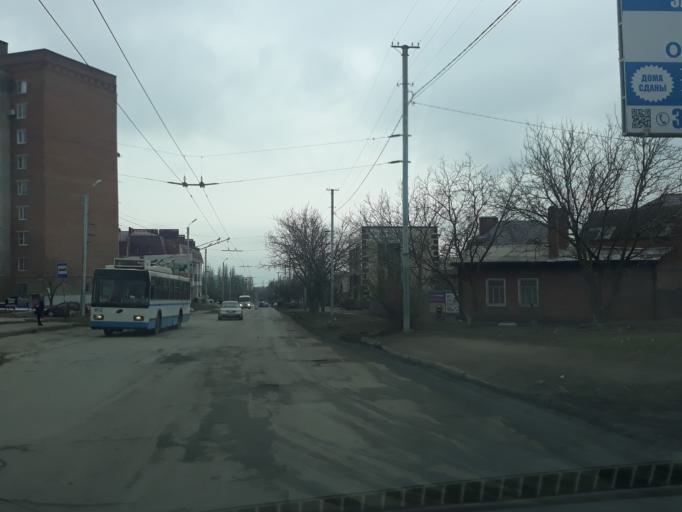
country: RU
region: Rostov
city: Taganrog
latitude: 47.2767
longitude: 38.9260
